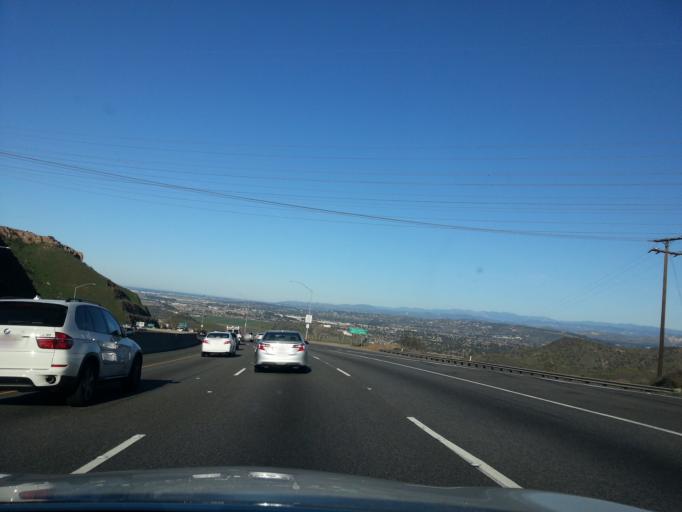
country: US
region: California
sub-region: Ventura County
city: Casa Conejo
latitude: 34.2001
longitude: -118.9575
